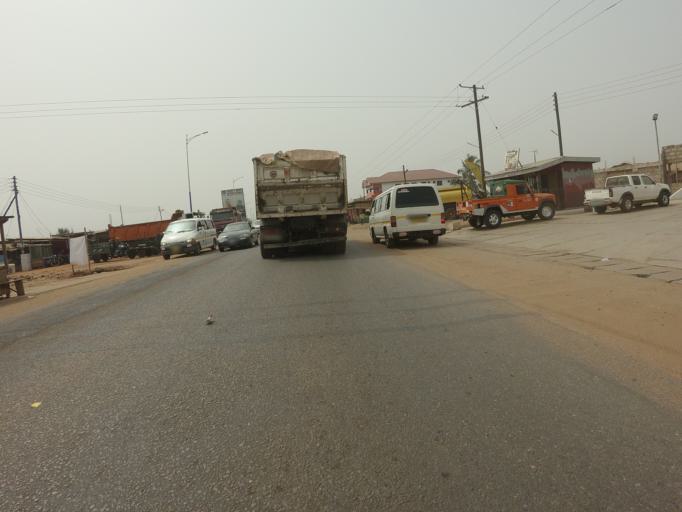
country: GH
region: Greater Accra
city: Tema
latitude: 5.7630
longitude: 0.0538
